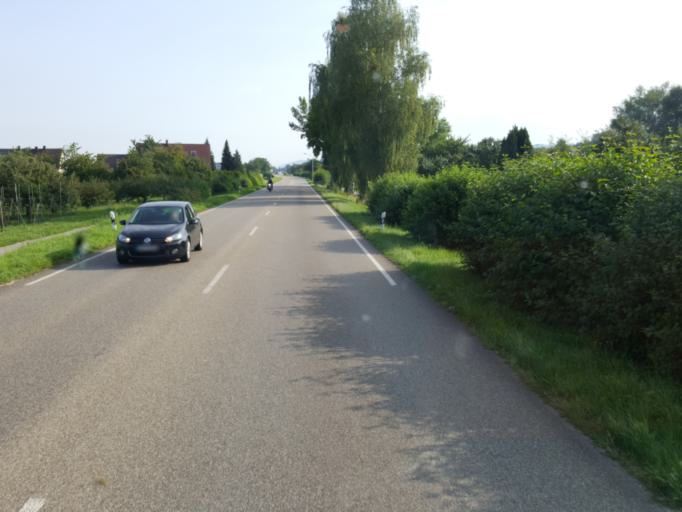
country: DE
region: Baden-Wuerttemberg
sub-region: Freiburg Region
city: Renchen
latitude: 48.6074
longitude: 8.0344
